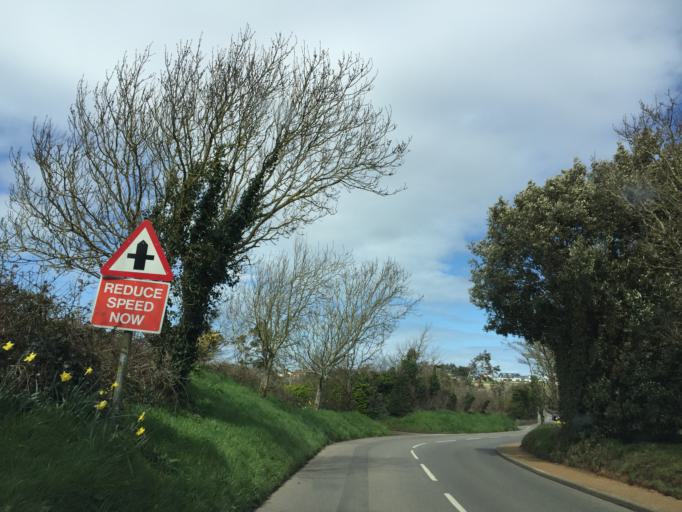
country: JE
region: St Helier
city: Saint Helier
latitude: 49.1758
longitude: -2.1729
